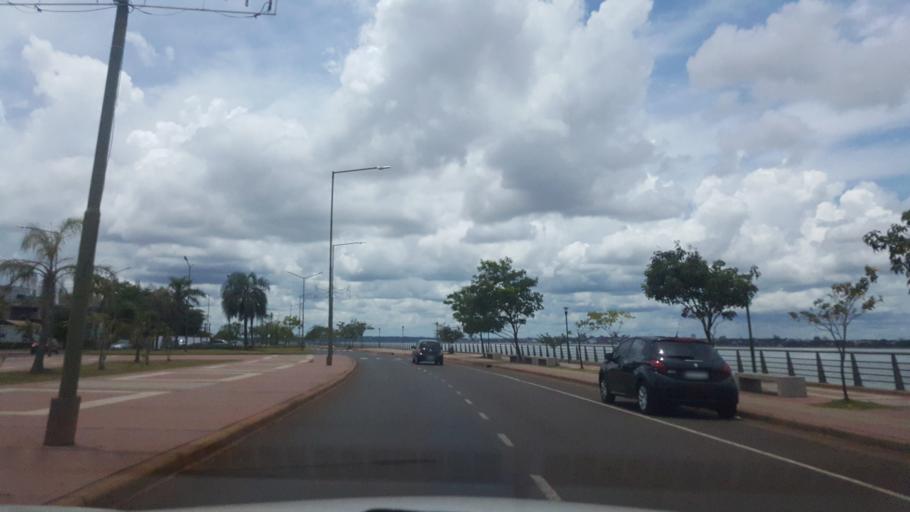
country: AR
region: Misiones
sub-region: Departamento de Capital
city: Posadas
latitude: -27.3690
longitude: -55.8844
